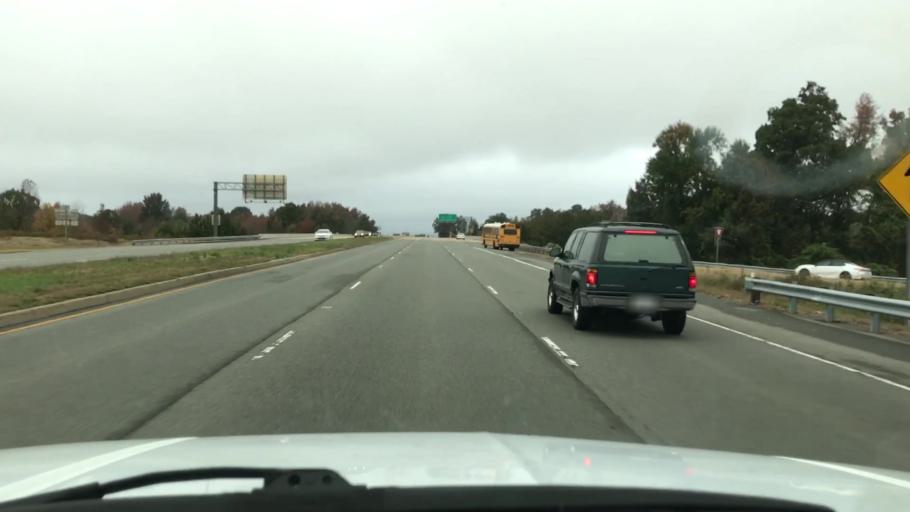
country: US
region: Virginia
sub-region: Henrico County
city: Chamberlayne
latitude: 37.6567
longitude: -77.4599
